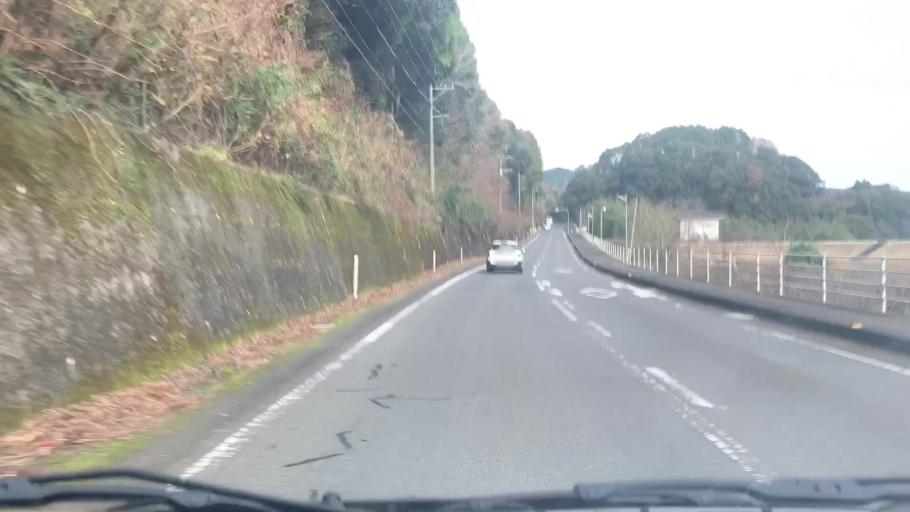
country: JP
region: Saga Prefecture
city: Imaricho-ko
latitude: 33.3169
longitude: 129.9695
